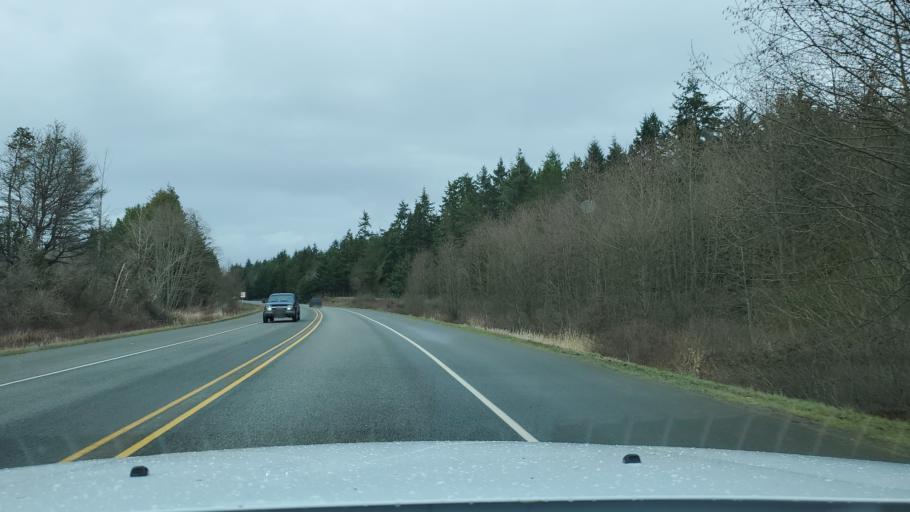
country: US
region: Washington
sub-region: Island County
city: Oak Harbor
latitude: 48.3260
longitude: -122.6413
